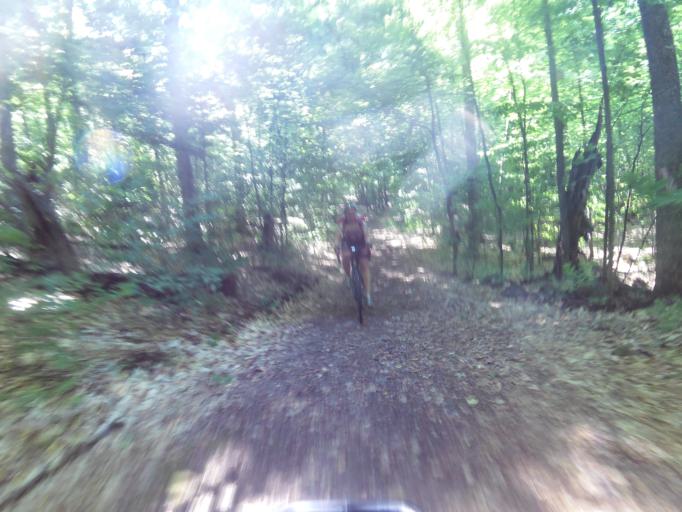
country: CA
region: Quebec
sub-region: Outaouais
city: Wakefield
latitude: 45.5490
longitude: -75.8929
